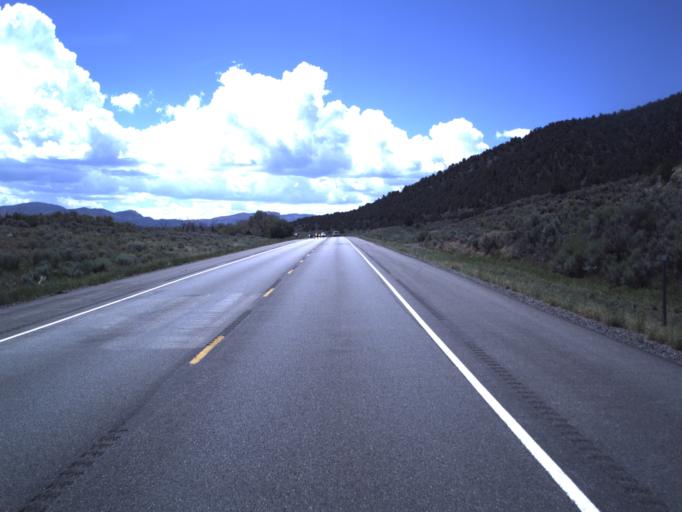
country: US
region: Utah
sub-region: Garfield County
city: Panguitch
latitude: 37.7973
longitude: -112.3985
